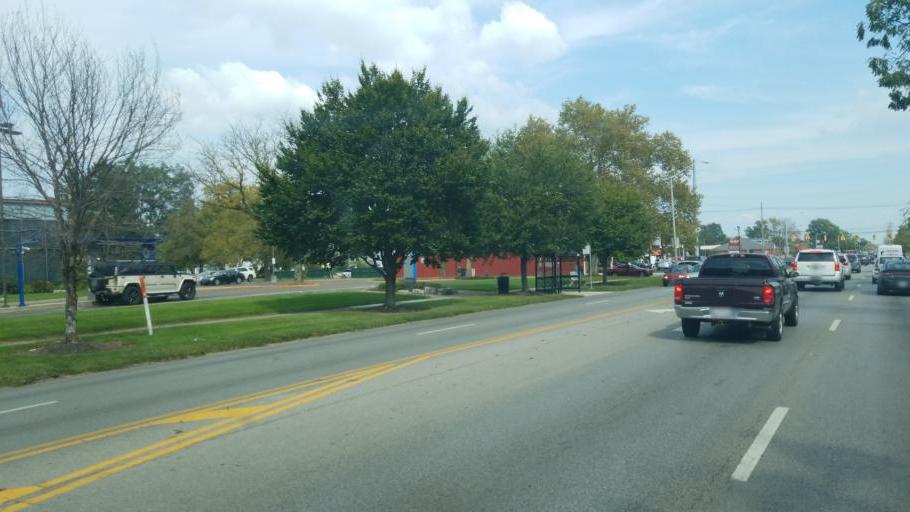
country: US
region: Ohio
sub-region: Franklin County
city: Bexley
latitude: 39.9717
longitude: -82.9157
